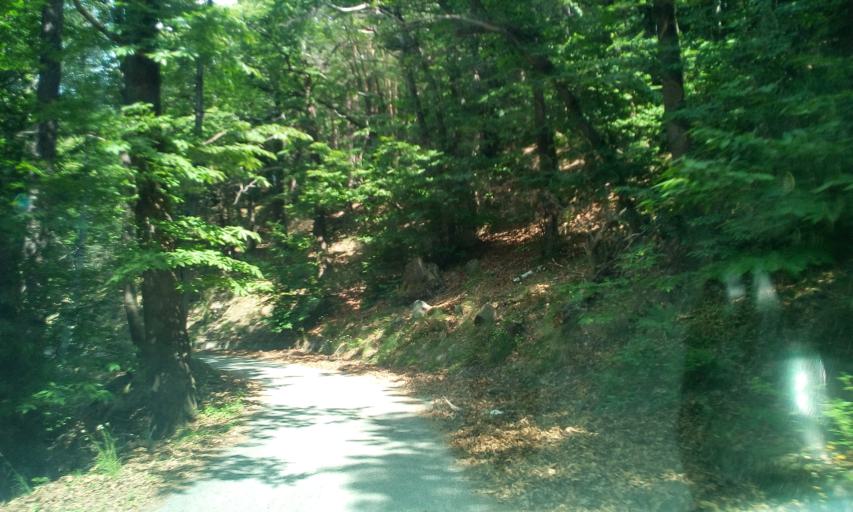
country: IT
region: Aosta Valley
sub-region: Valle d'Aosta
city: Chatillon
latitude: 45.7314
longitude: 7.6322
